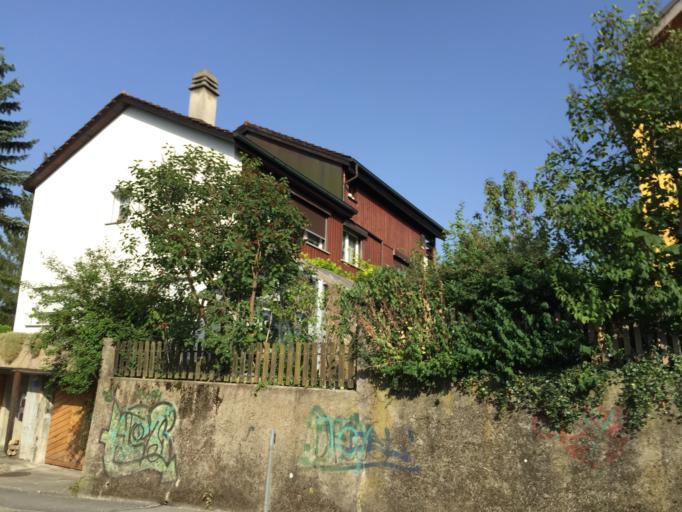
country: CH
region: Bern
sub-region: Bern-Mittelland District
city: Bern
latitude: 46.9301
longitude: 7.4532
